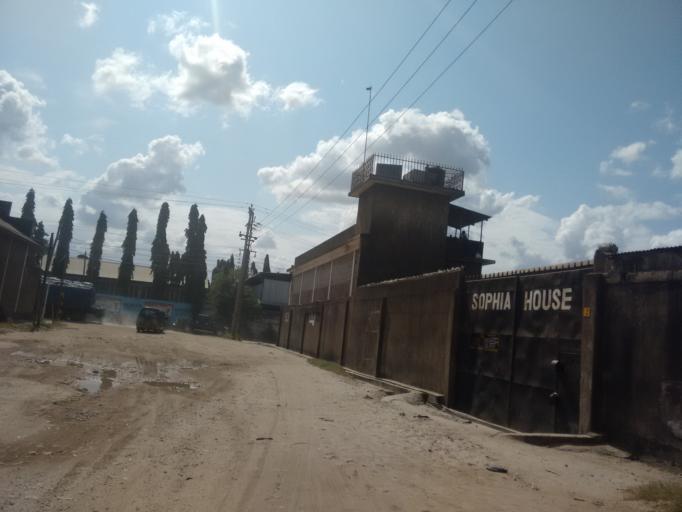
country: TZ
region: Dar es Salaam
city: Dar es Salaam
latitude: -6.8383
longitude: 39.2697
